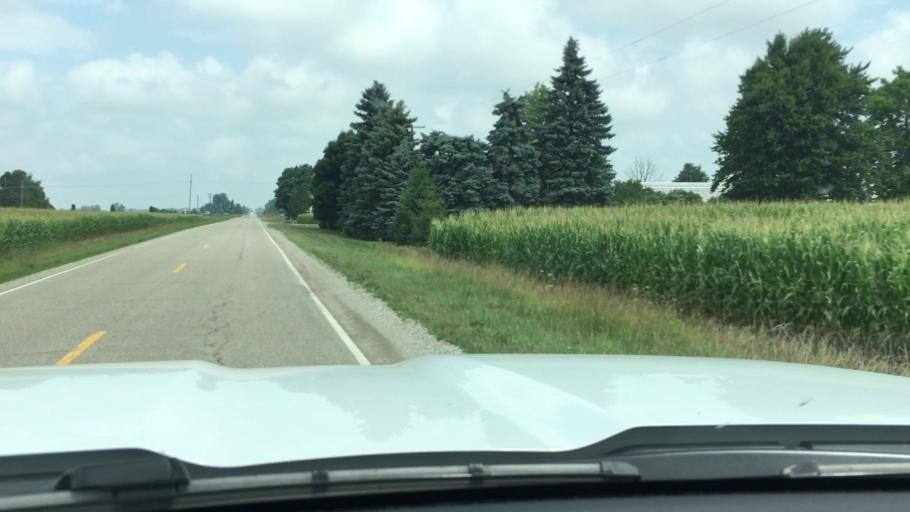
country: US
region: Michigan
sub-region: Sanilac County
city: Marlette
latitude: 43.3848
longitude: -83.0069
